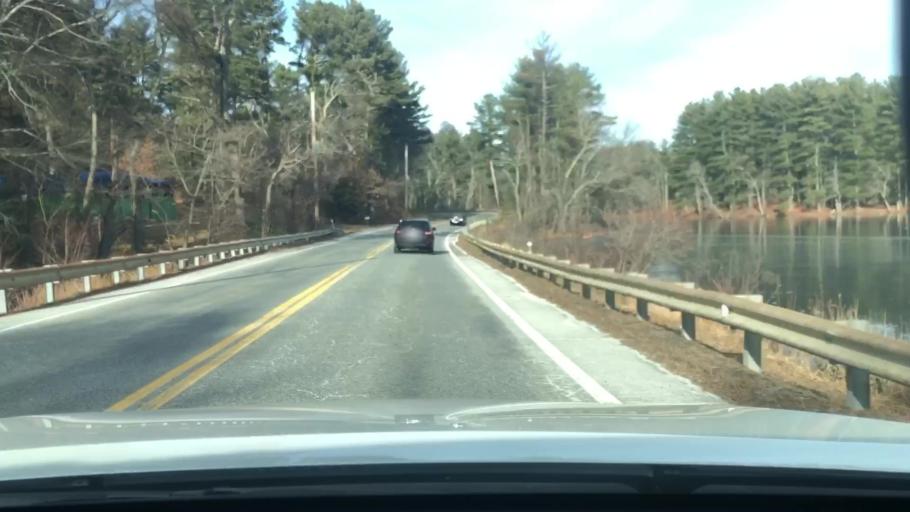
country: US
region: Massachusetts
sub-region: Worcester County
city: Grafton
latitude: 42.1932
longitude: -71.6563
